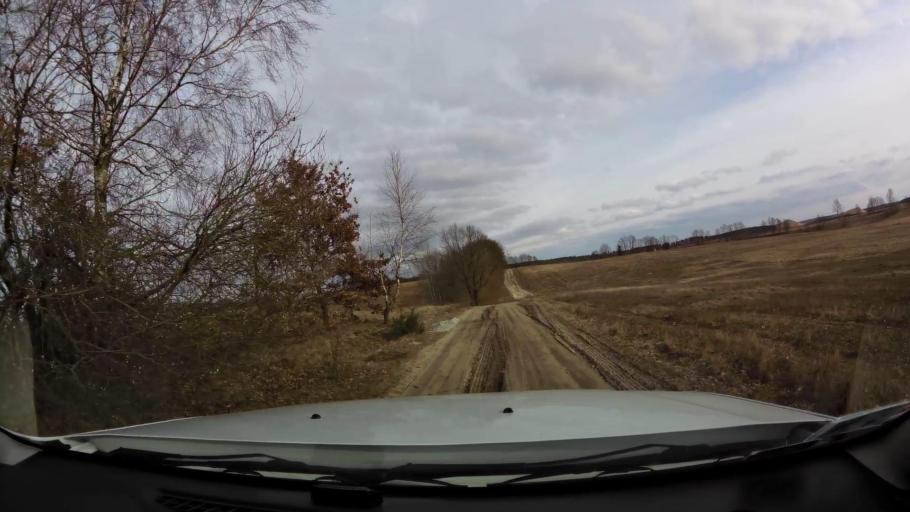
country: PL
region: West Pomeranian Voivodeship
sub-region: Powiat drawski
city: Drawsko Pomorskie
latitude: 53.5118
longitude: 15.7576
